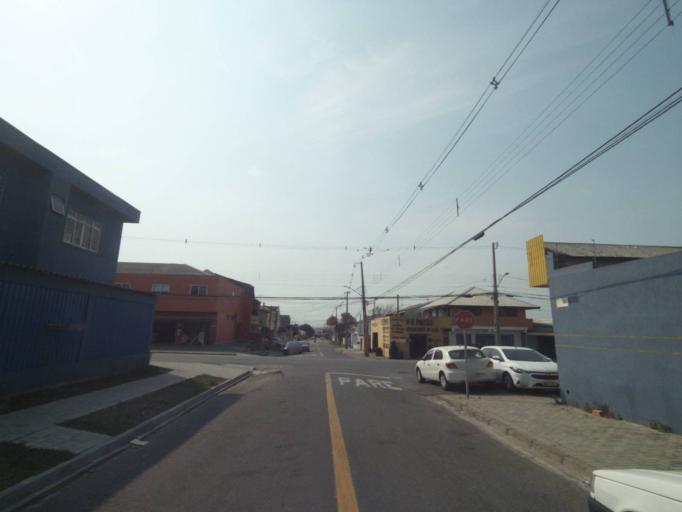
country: BR
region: Parana
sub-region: Sao Jose Dos Pinhais
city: Sao Jose dos Pinhais
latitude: -25.4887
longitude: -49.2048
